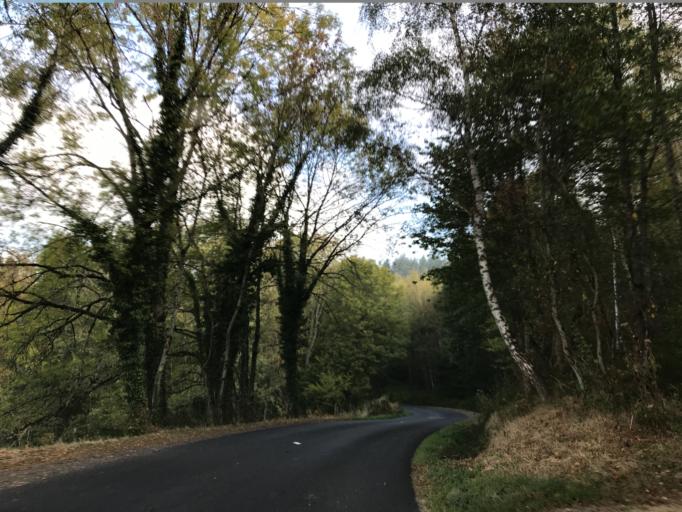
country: FR
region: Auvergne
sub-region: Departement du Puy-de-Dome
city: Escoutoux
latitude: 45.7935
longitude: 3.6153
